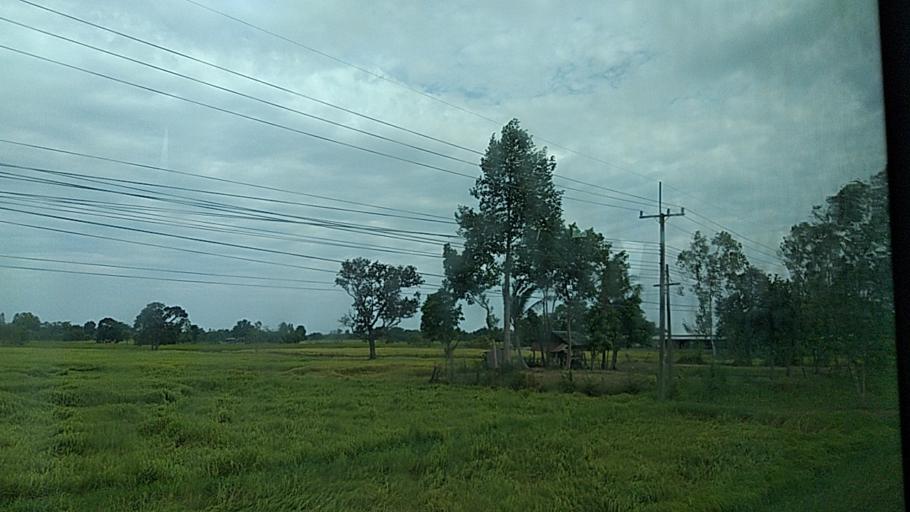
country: TH
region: Maha Sarakham
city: Kantharawichai
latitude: 16.3295
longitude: 103.2595
